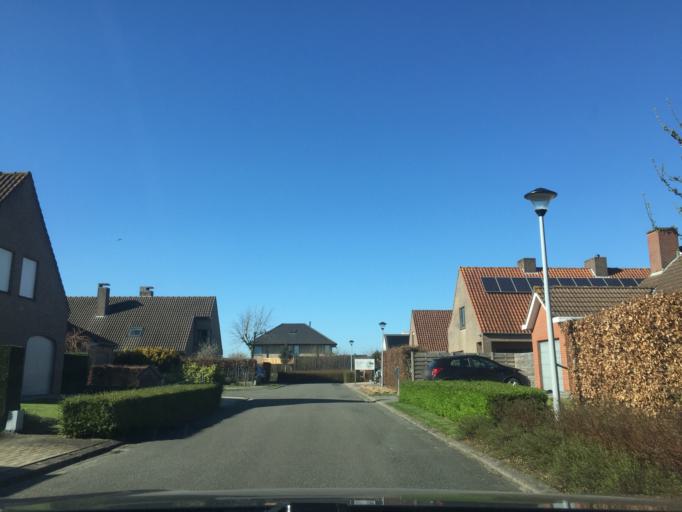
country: BE
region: Flanders
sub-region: Provincie West-Vlaanderen
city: Hooglede
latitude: 50.9809
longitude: 3.0857
